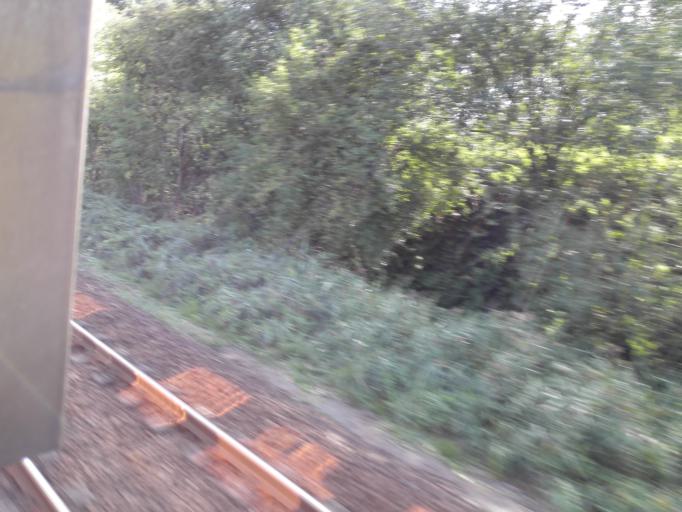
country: BE
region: Flanders
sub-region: Provincie Vlaams-Brabant
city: Rotselaar
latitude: 50.9206
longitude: 4.7037
